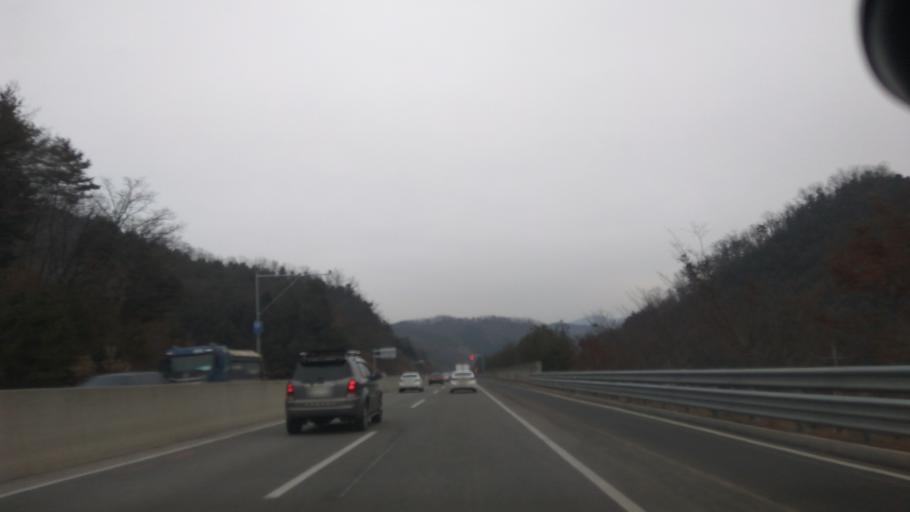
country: KR
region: Gangwon-do
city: Sindong
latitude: 37.7409
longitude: 127.6681
